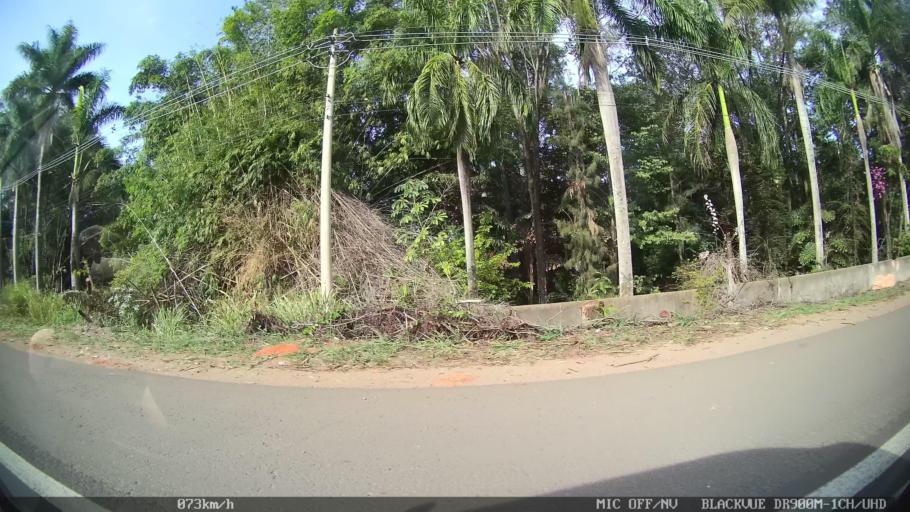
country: BR
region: Sao Paulo
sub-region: Piracicaba
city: Piracicaba
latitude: -22.6826
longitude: -47.6905
